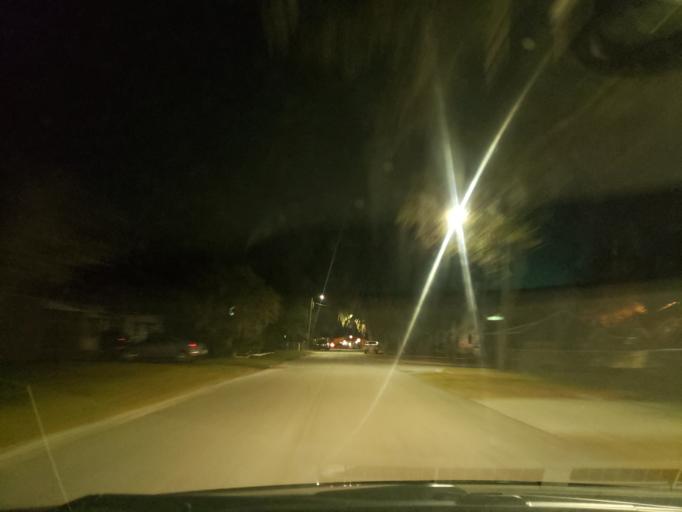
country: US
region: Georgia
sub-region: Chatham County
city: Savannah
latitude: 32.0390
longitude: -81.1125
